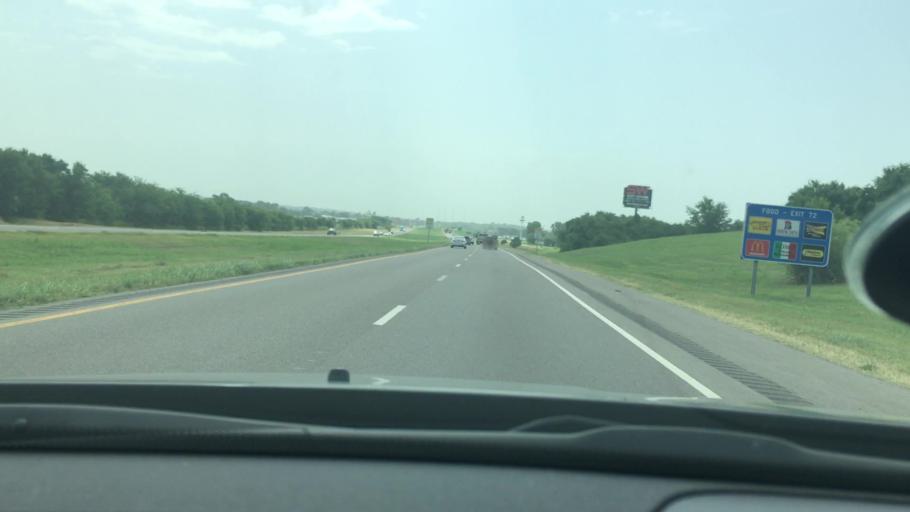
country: US
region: Oklahoma
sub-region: Garvin County
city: Pauls Valley
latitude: 34.7521
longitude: -97.2763
